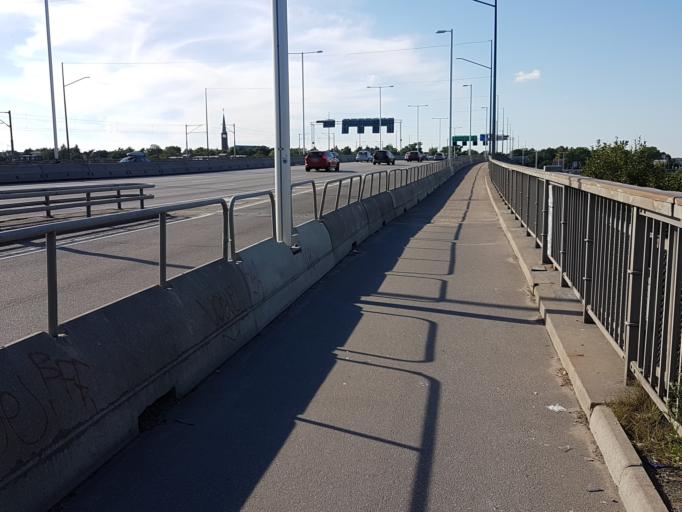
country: SE
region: Stockholm
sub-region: Solna Kommun
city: Solna
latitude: 59.3172
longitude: 18.0008
